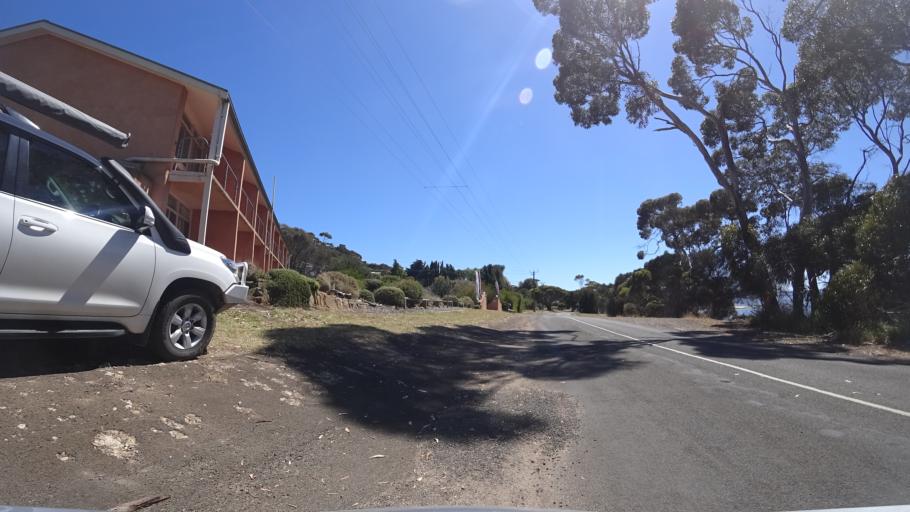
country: AU
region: South Australia
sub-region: Kangaroo Island
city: Kingscote
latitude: -35.7757
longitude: 137.7771
